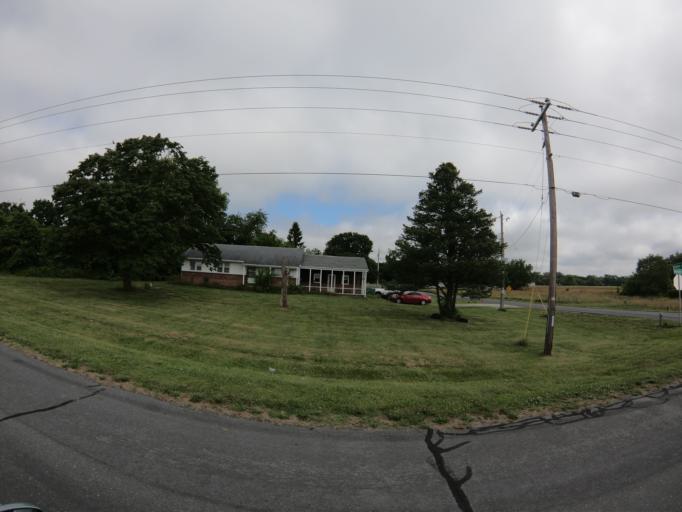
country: US
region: Delaware
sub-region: Kent County
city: Riverview
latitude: 39.0114
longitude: -75.5138
